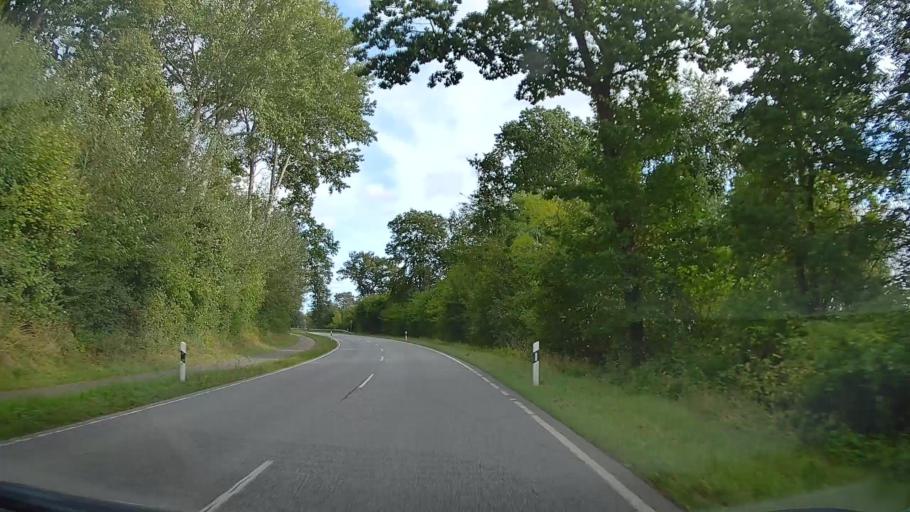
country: DE
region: Schleswig-Holstein
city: Niesgrau
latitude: 54.7504
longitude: 9.8500
